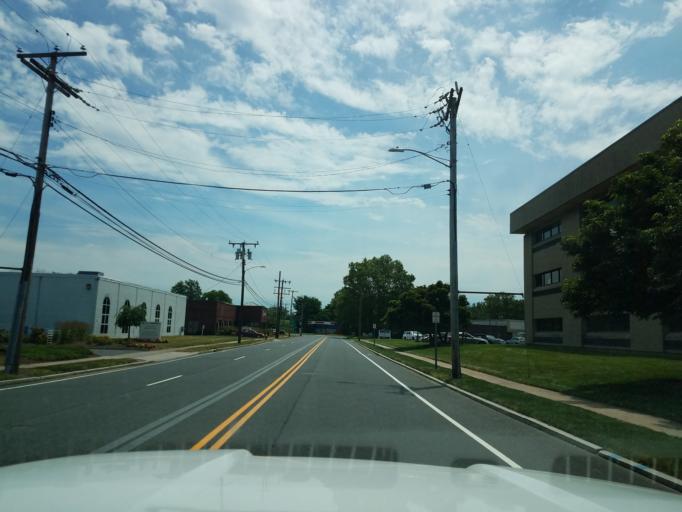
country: US
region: Connecticut
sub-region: Hartford County
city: Hartford
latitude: 41.7643
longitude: -72.6583
